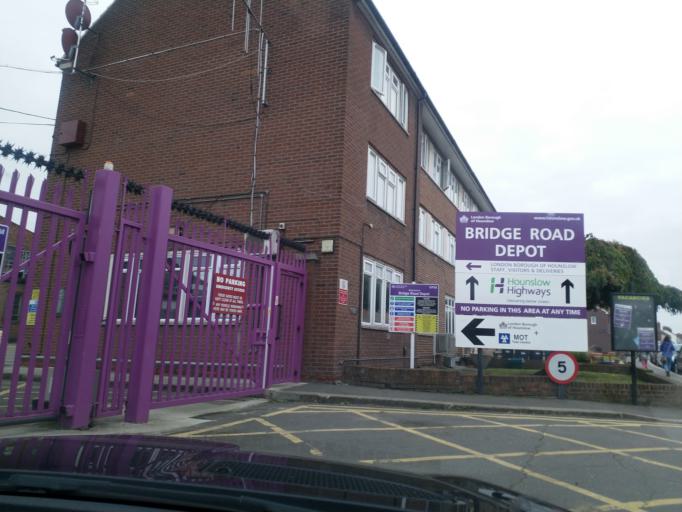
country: GB
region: England
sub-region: Greater London
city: Isleworth
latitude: 51.4701
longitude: -0.3492
